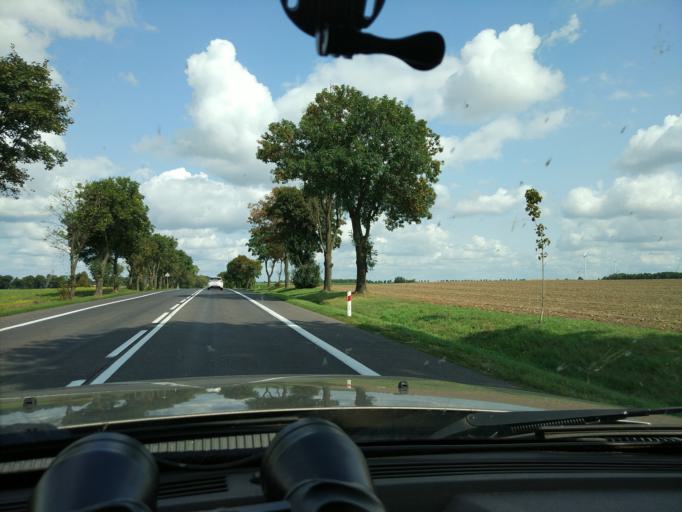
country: PL
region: Masovian Voivodeship
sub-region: Powiat mlawski
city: Wisniewo
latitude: 53.0437
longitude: 20.3417
